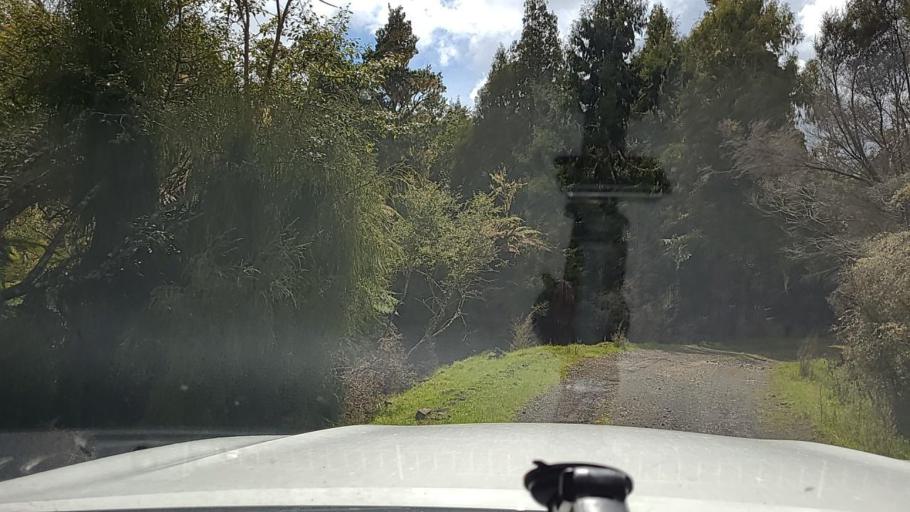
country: NZ
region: Bay of Plenty
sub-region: Opotiki District
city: Opotiki
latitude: -38.2041
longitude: 177.6096
